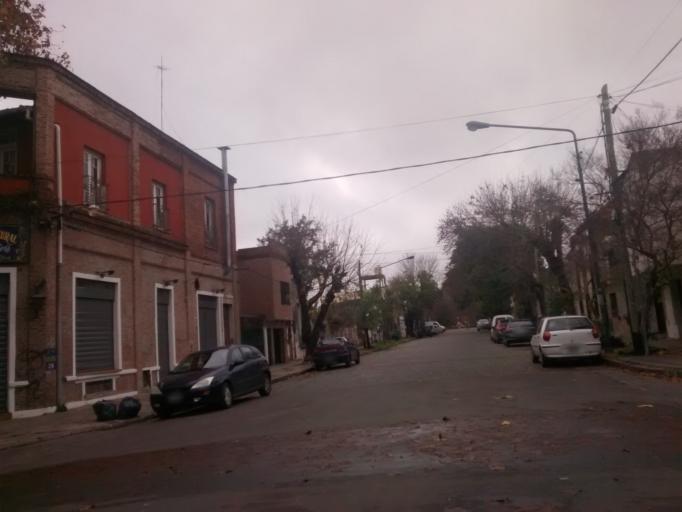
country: AR
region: Buenos Aires
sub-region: Partido de La Plata
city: La Plata
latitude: -34.8998
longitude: -57.9537
